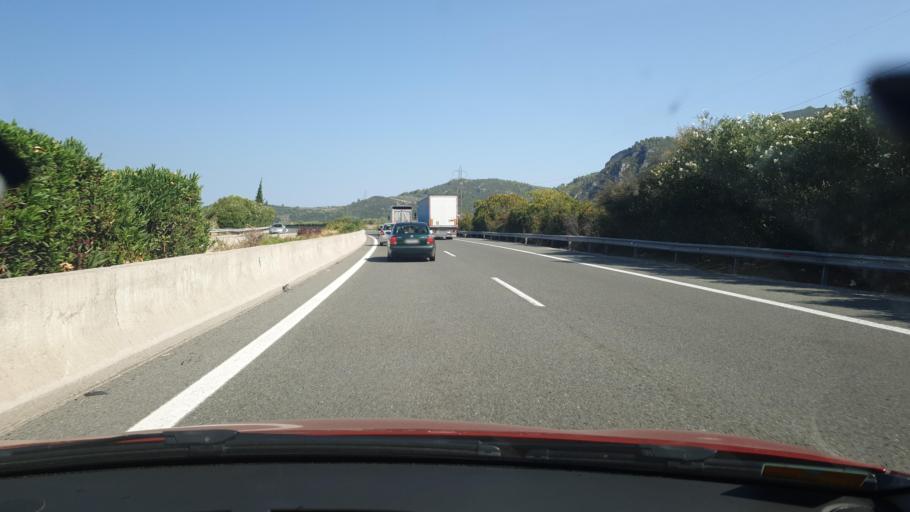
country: GR
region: Central Greece
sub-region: Nomos Fthiotidos
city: Livanates
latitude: 38.7393
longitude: 22.9942
